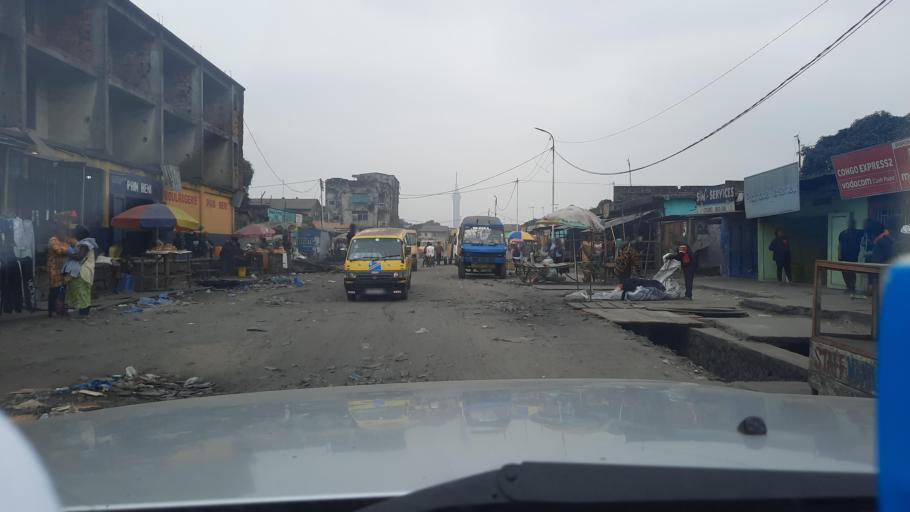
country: CD
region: Kinshasa
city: Masina
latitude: -4.3894
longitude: 15.3469
